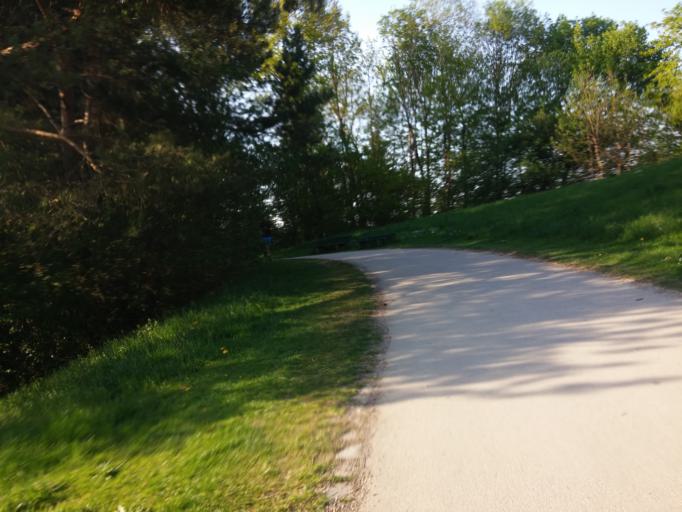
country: DE
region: Bavaria
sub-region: Upper Bavaria
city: Neubiberg
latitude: 48.1145
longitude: 11.6421
